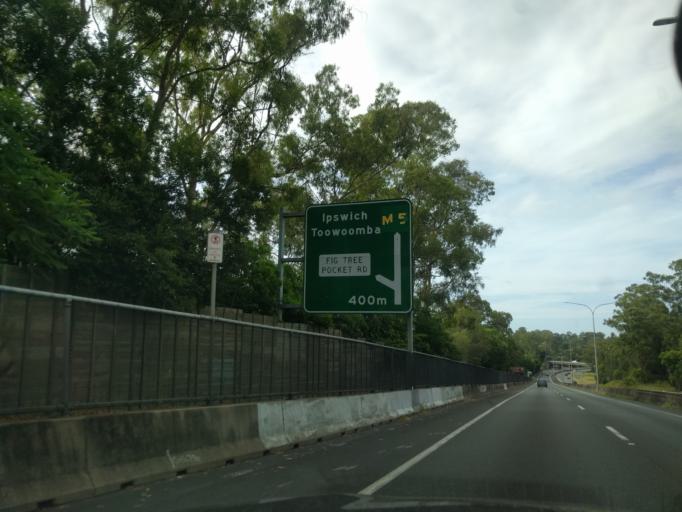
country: AU
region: Queensland
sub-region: Brisbane
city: Kenmore Hills
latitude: -27.5130
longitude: 152.9575
